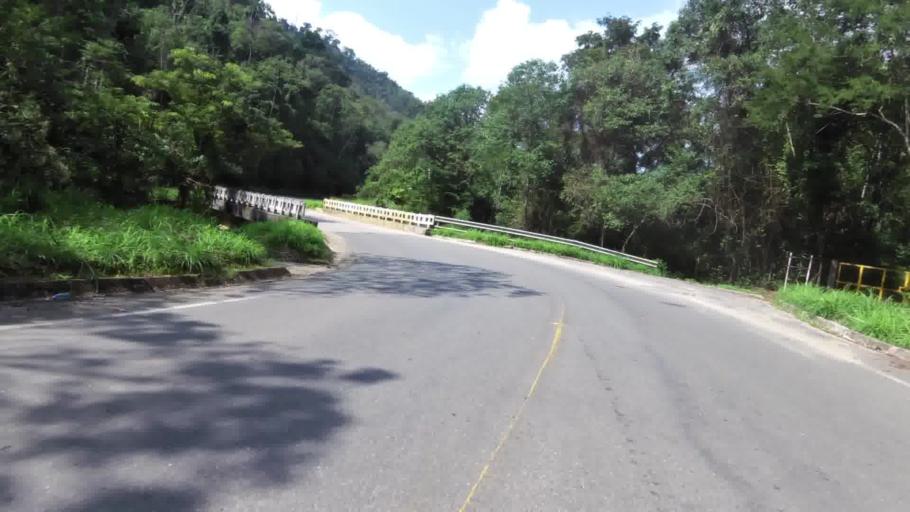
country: BR
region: Espirito Santo
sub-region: Alfredo Chaves
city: Alfredo Chaves
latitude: -20.6073
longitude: -40.7889
